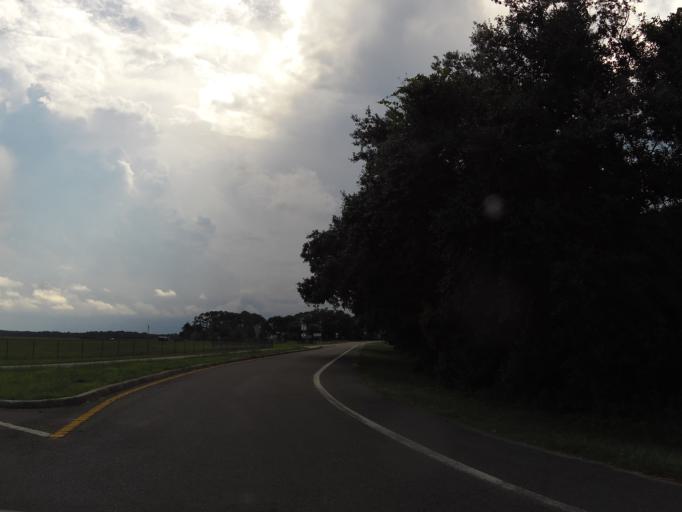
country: US
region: Florida
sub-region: Nassau County
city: Fernandina Beach
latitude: 30.6189
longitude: -81.4553
